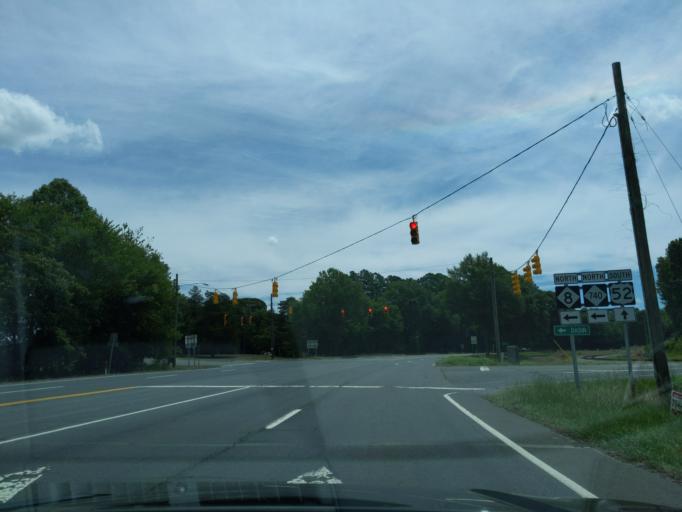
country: US
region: North Carolina
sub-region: Stanly County
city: Albemarle
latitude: 35.4442
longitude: -80.2240
